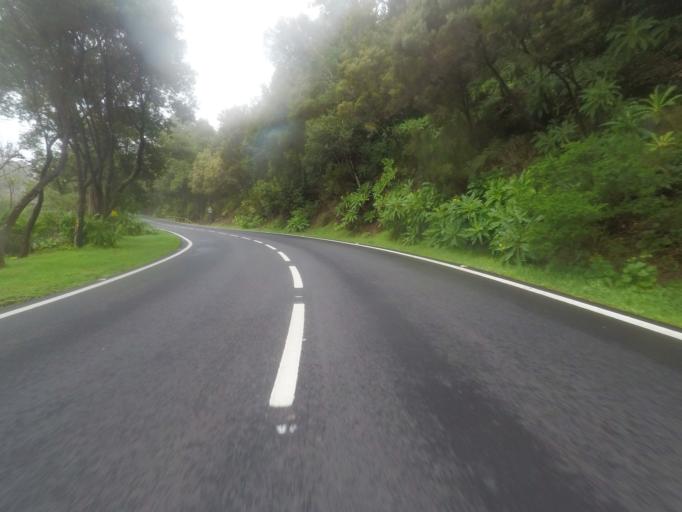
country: ES
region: Canary Islands
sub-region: Provincia de Santa Cruz de Tenerife
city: Alajero
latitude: 28.1196
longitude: -17.2478
